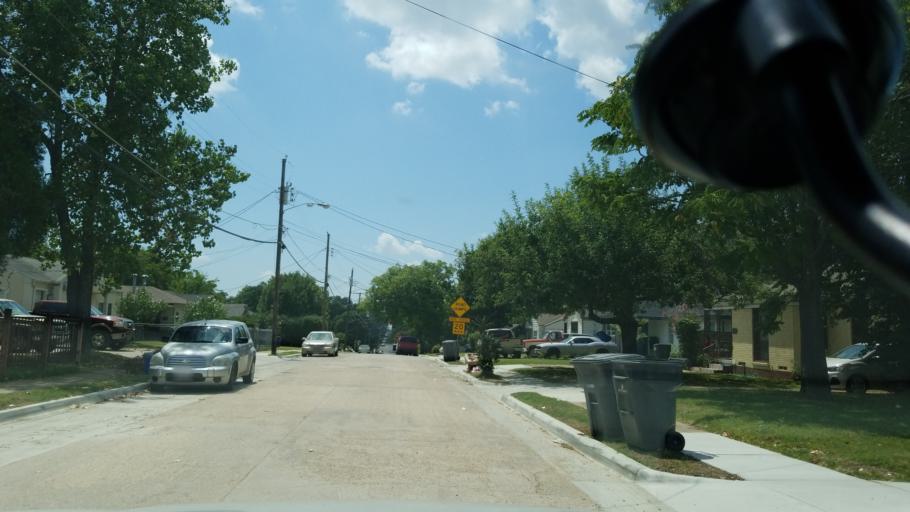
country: US
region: Texas
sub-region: Dallas County
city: Cockrell Hill
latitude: 32.7283
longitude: -96.8745
